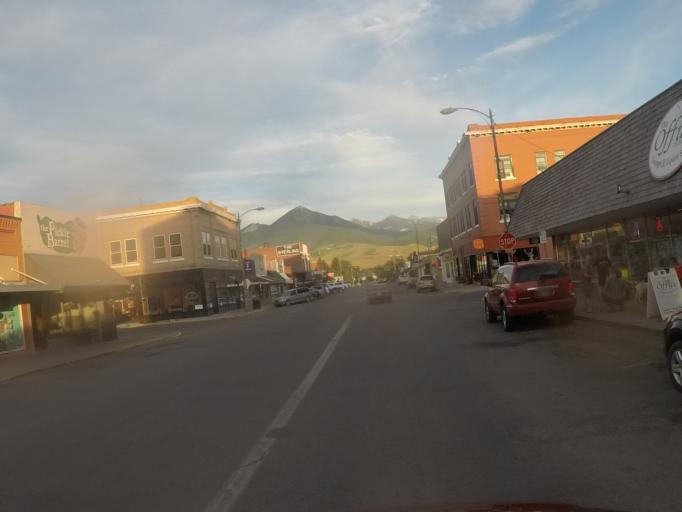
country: US
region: Montana
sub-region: Park County
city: Livingston
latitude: 45.6607
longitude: -110.5593
